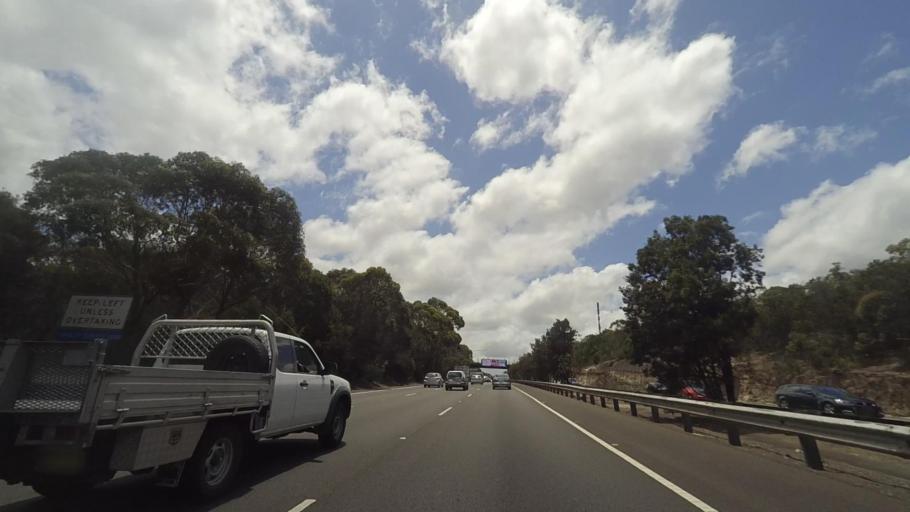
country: AU
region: New South Wales
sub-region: Hornsby Shire
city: Mount Colah
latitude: -33.6809
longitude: 151.1203
